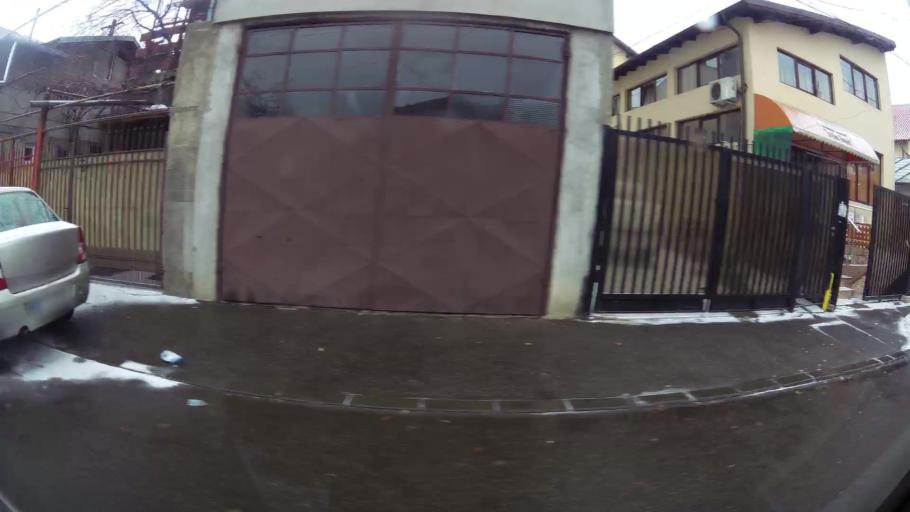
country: RO
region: Prahova
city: Ploiesti
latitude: 44.9507
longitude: 26.0127
